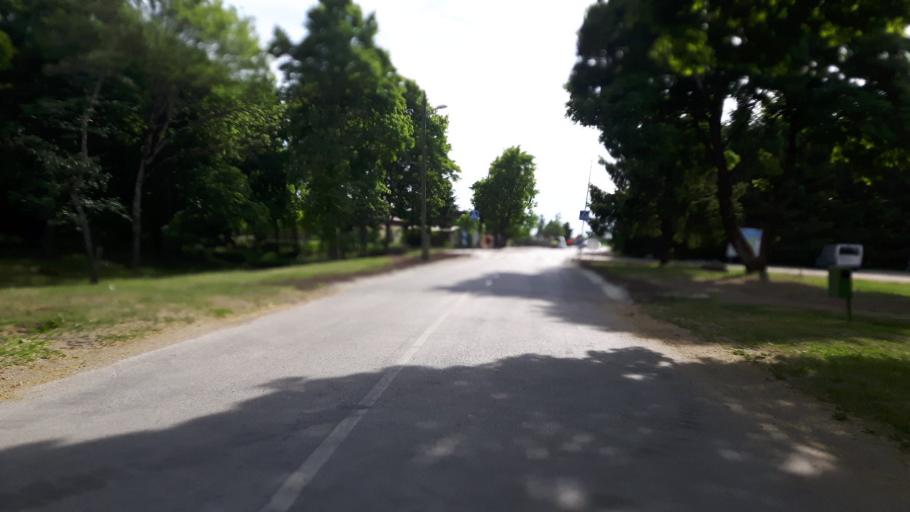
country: EE
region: Harju
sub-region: Raasiku vald
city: Arukula
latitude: 59.4279
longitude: 25.0950
